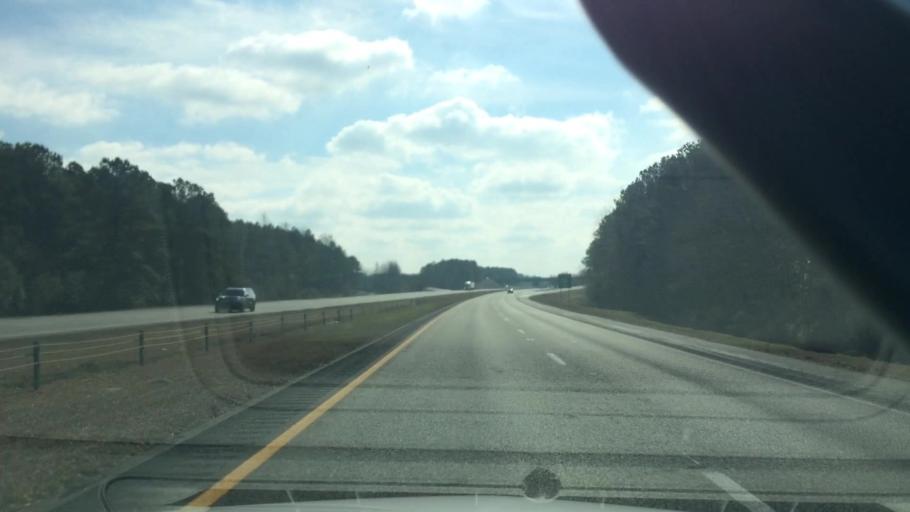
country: US
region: North Carolina
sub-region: Duplin County
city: Wallace
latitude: 34.6932
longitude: -77.9451
